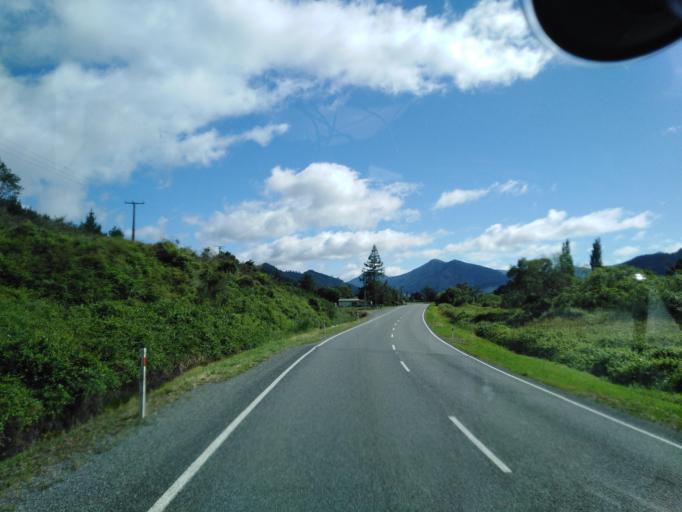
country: NZ
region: Nelson
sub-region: Nelson City
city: Nelson
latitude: -41.2453
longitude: 173.5768
